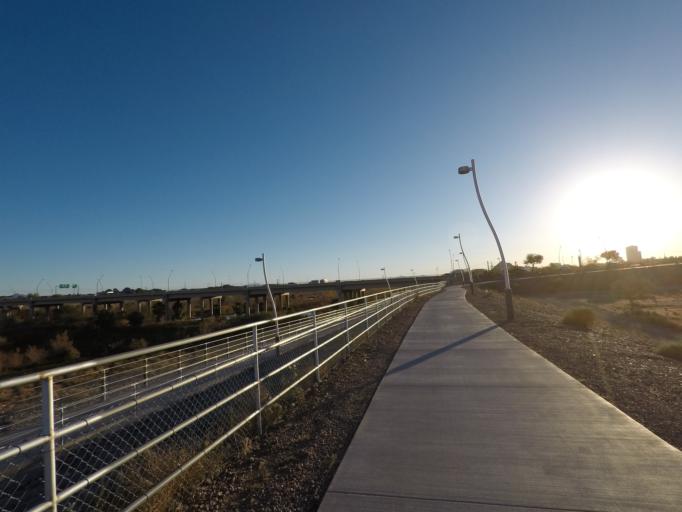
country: US
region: Arizona
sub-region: Maricopa County
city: Tempe Junction
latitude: 33.4341
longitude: -111.9626
